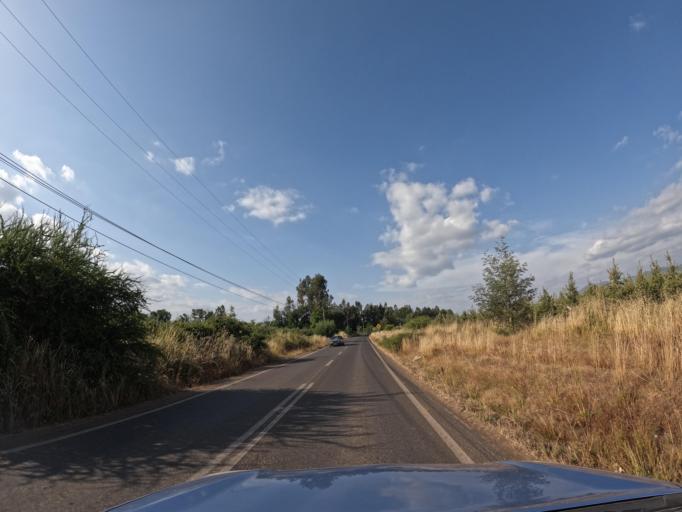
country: CL
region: Maule
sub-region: Provincia de Curico
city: Molina
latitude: -35.2625
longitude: -71.2443
